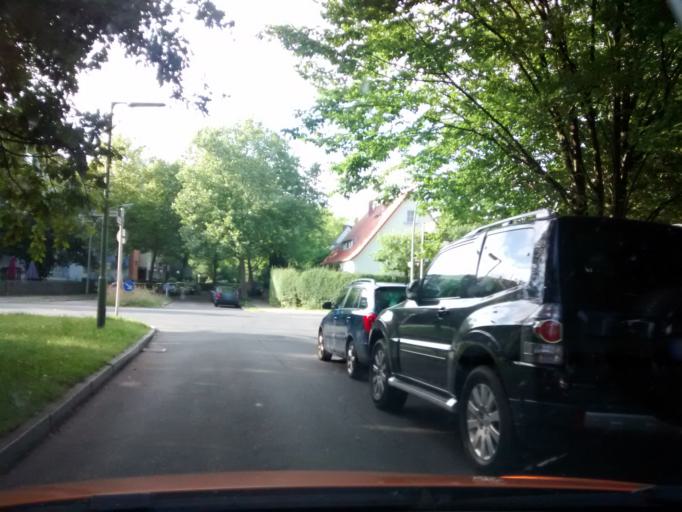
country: DE
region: Berlin
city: Marienfelde
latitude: 52.4252
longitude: 13.3619
